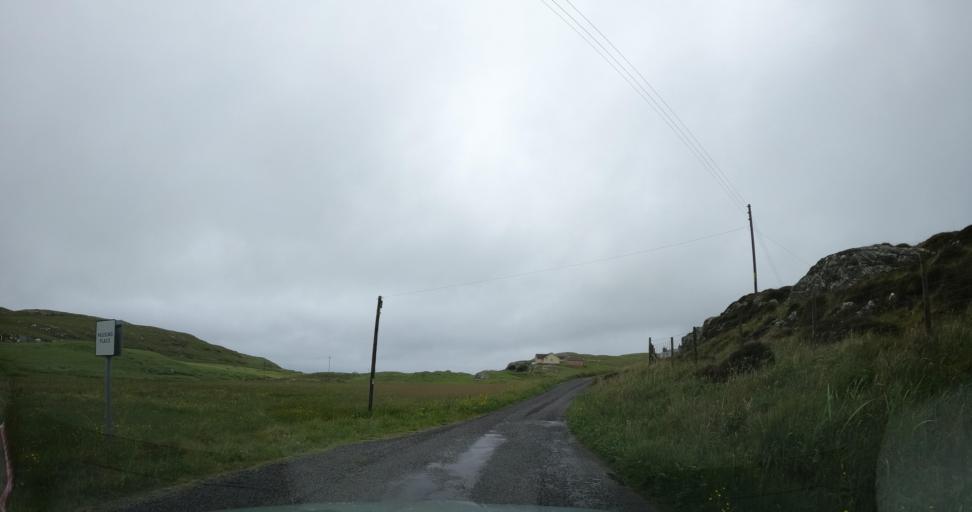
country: GB
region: Scotland
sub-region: Eilean Siar
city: Barra
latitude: 57.0042
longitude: -7.4893
